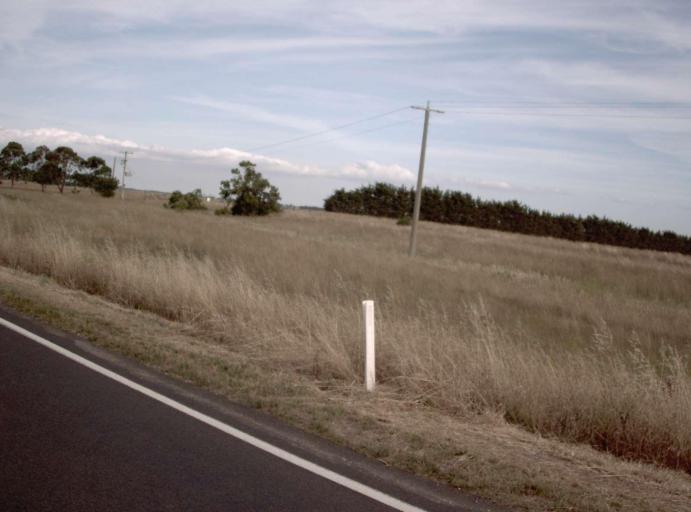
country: AU
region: Victoria
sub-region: Wellington
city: Heyfield
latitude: -38.0197
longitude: 146.7342
